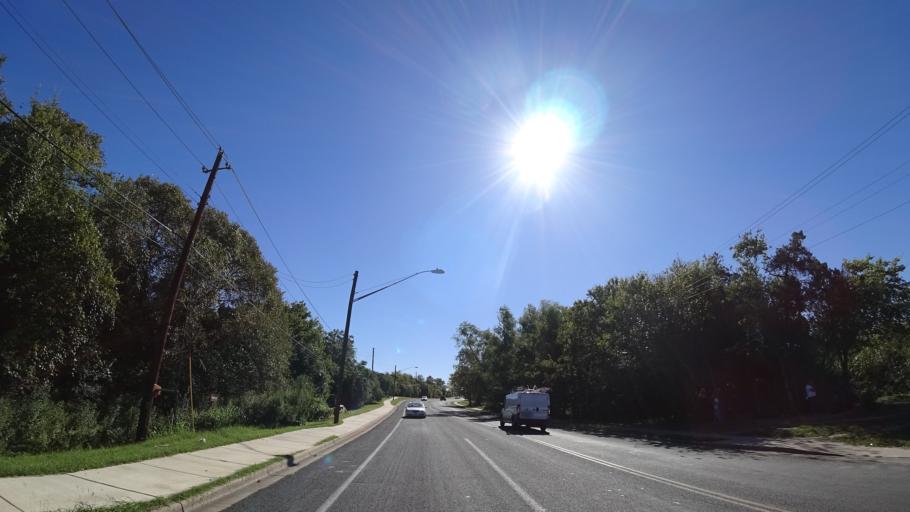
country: US
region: Texas
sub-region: Travis County
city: Austin
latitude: 30.2248
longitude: -97.7499
